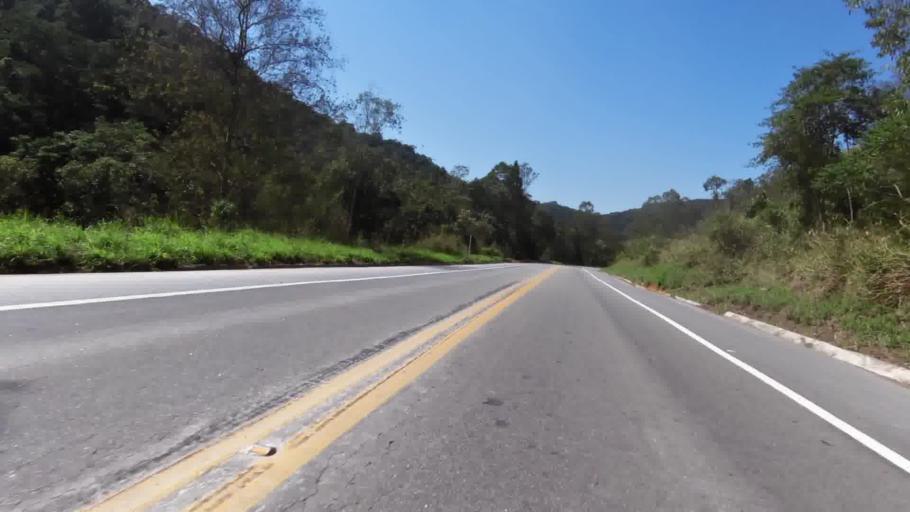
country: BR
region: Espirito Santo
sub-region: Marechal Floriano
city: Marechal Floriano
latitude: -20.4130
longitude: -40.8531
